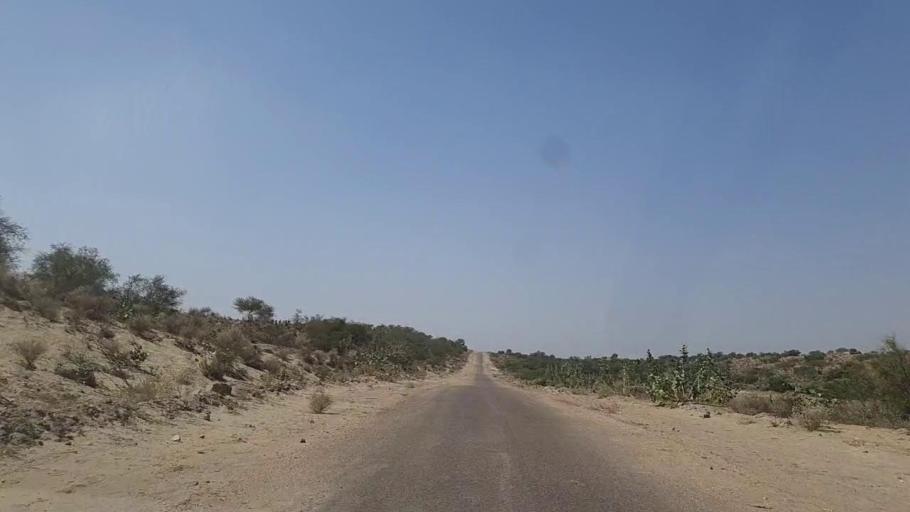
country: PK
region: Sindh
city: Diplo
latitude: 24.5518
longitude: 69.4312
